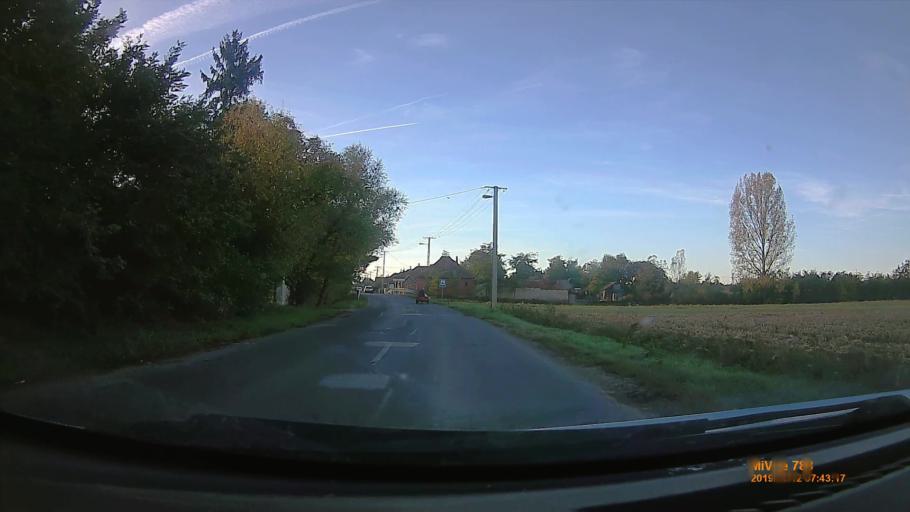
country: RO
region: Bihor
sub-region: Comuna Bors
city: Bors
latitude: 47.1944
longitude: 21.7877
